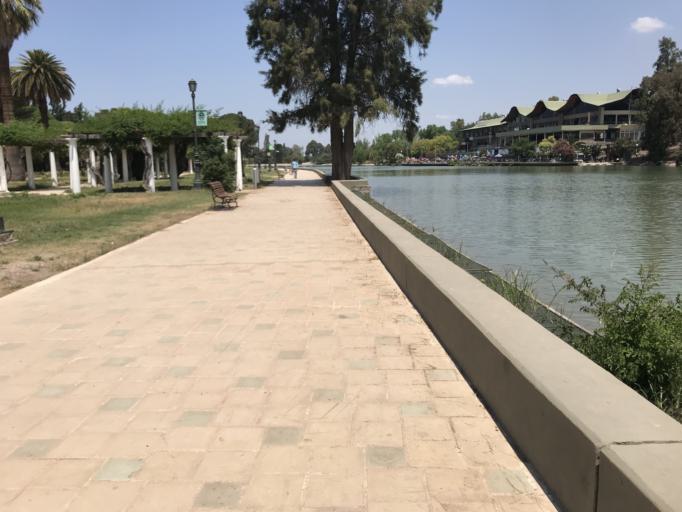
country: AR
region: Mendoza
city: Mendoza
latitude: -32.8915
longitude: -68.8670
